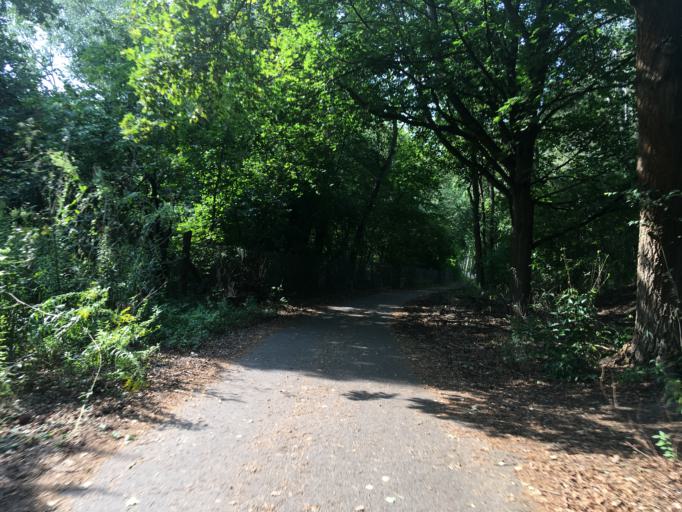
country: DE
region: Berlin
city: Falkenhagener Feld
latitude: 52.5986
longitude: 13.1642
